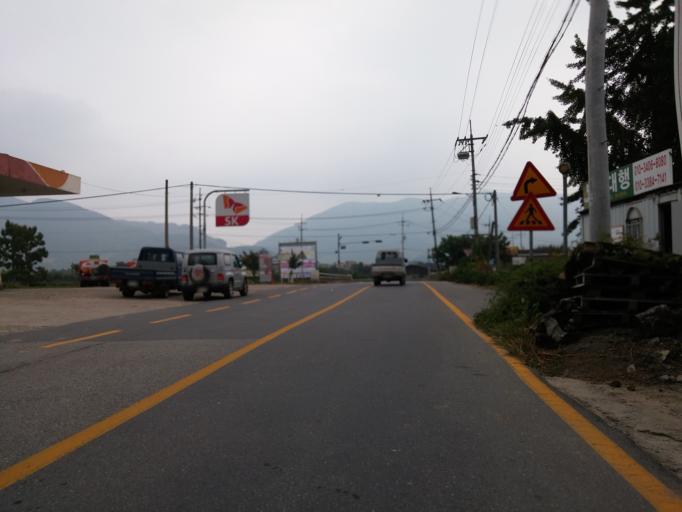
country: KR
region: Chungcheongbuk-do
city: Okcheon
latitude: 36.3946
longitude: 127.7329
